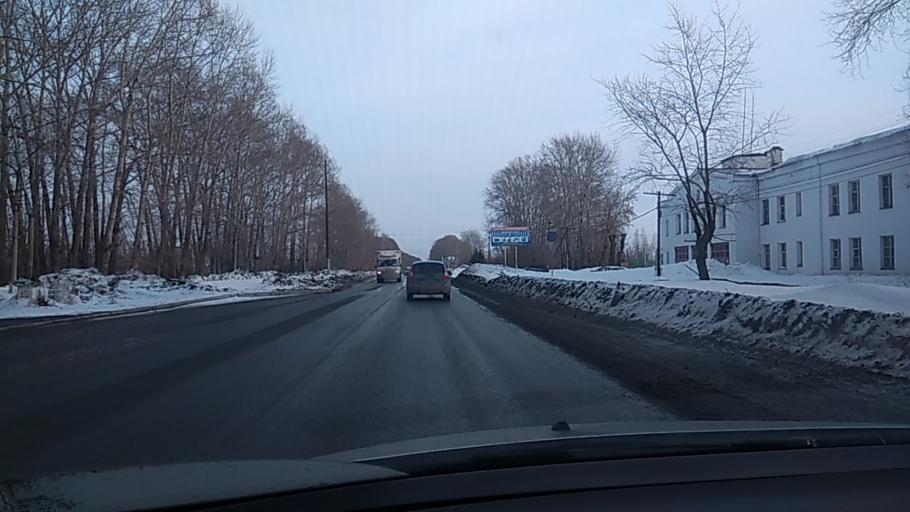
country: RU
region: Sverdlovsk
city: Martyush
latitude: 56.4451
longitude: 61.8202
